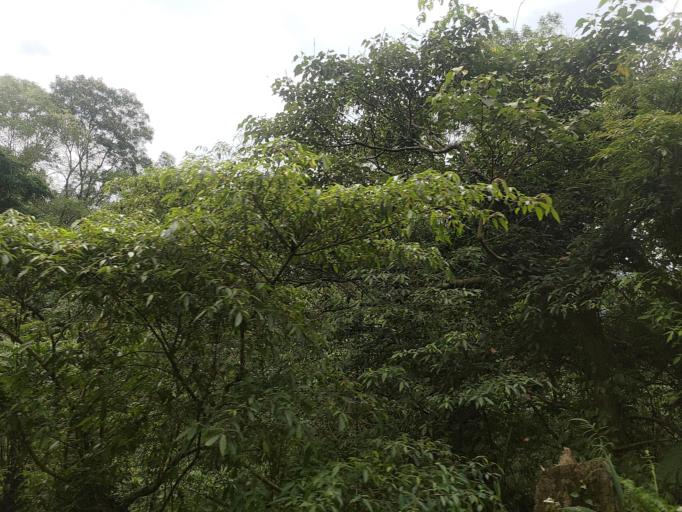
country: TW
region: Taiwan
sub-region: Hsinchu
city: Hsinchu
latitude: 24.6325
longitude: 121.0714
